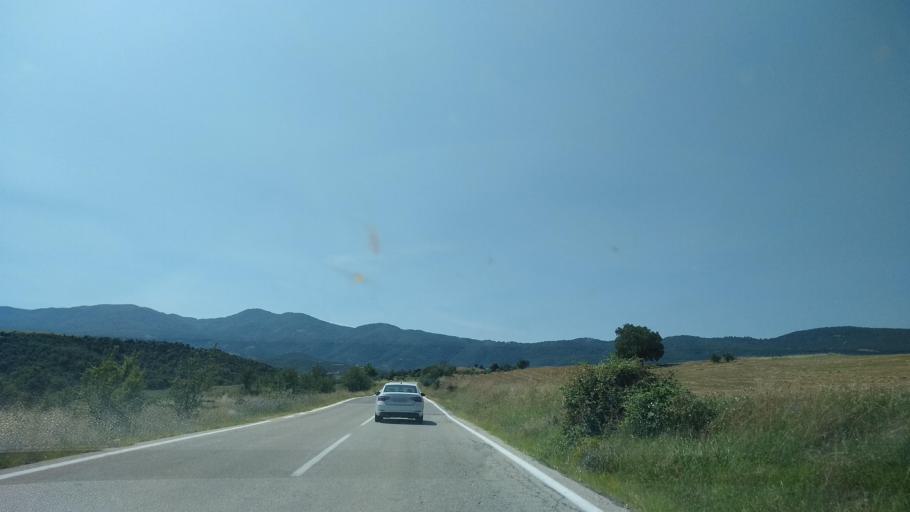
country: GR
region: Central Macedonia
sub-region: Nomos Thessalonikis
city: Nea Apollonia
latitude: 40.5217
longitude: 23.4719
